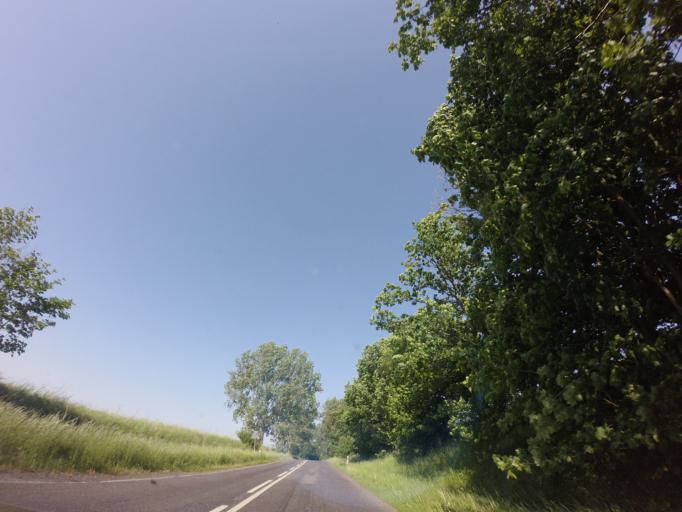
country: PL
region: West Pomeranian Voivodeship
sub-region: Powiat stargardzki
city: Kobylanka
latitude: 53.3102
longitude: 14.8352
